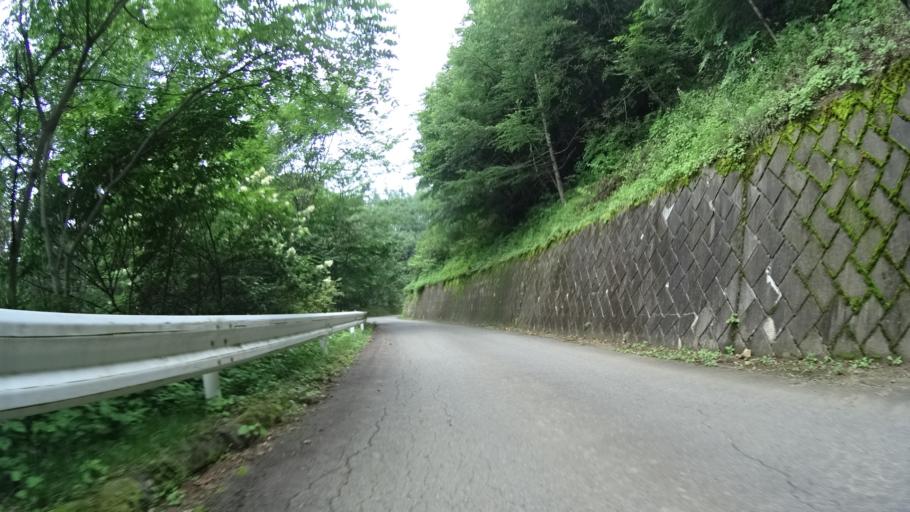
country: JP
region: Nagano
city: Saku
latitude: 36.0952
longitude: 138.6820
